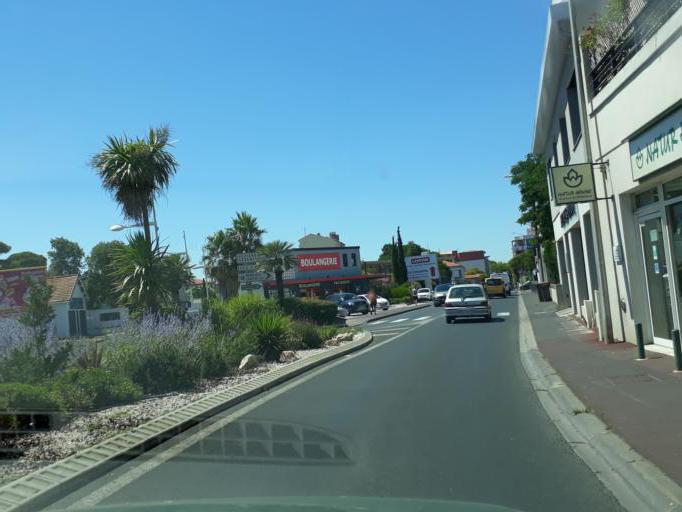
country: FR
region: Languedoc-Roussillon
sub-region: Departement de l'Herault
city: Agde
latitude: 43.3113
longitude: 3.4774
